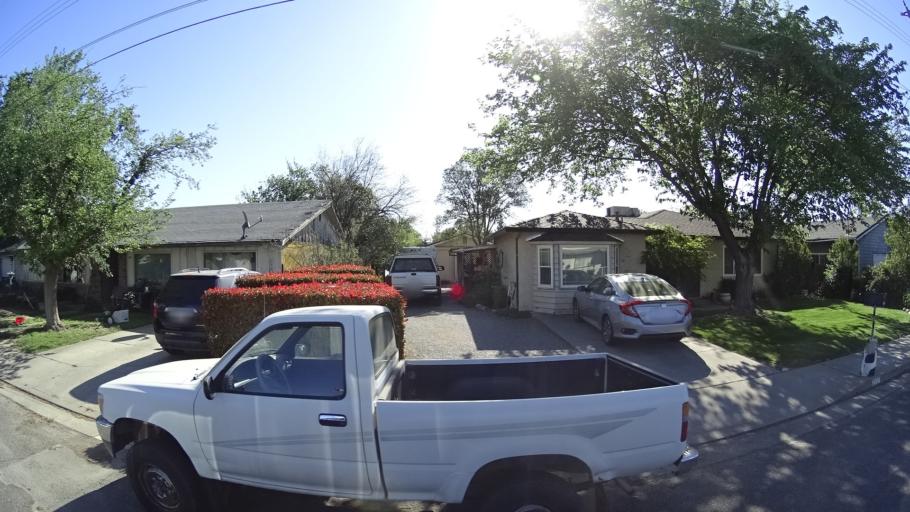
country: US
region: California
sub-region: Glenn County
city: Orland
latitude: 39.7528
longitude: -122.1850
